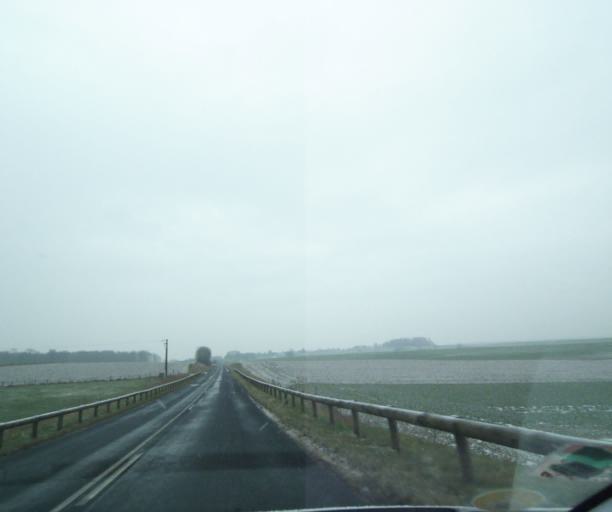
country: FR
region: Champagne-Ardenne
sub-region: Departement de la Haute-Marne
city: Wassy
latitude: 48.4703
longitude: 5.0236
